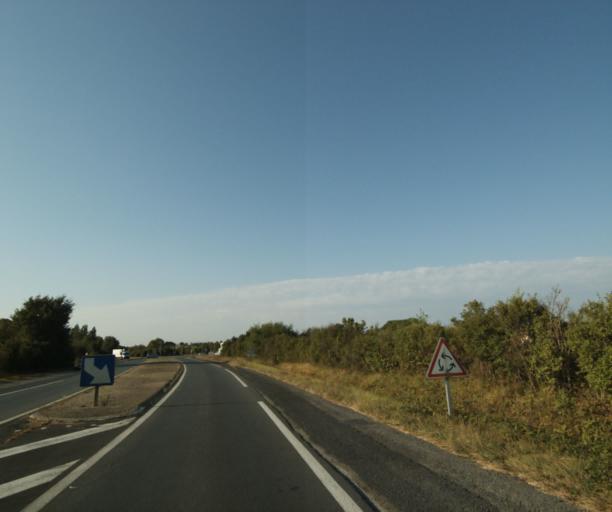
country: FR
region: Poitou-Charentes
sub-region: Departement de la Charente-Maritime
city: Saint-Hippolyte
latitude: 45.9187
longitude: -0.8860
